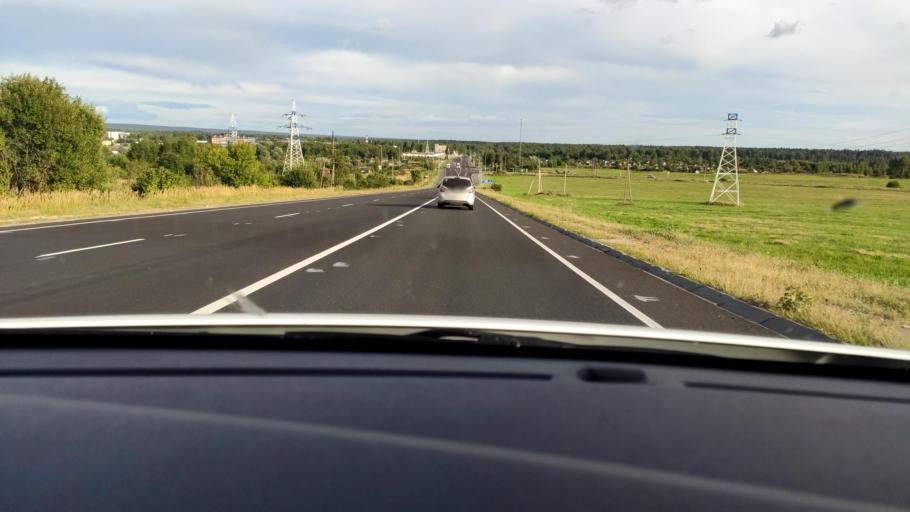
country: RU
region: Mariy-El
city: Krasnogorskiy
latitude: 56.1719
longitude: 48.2785
